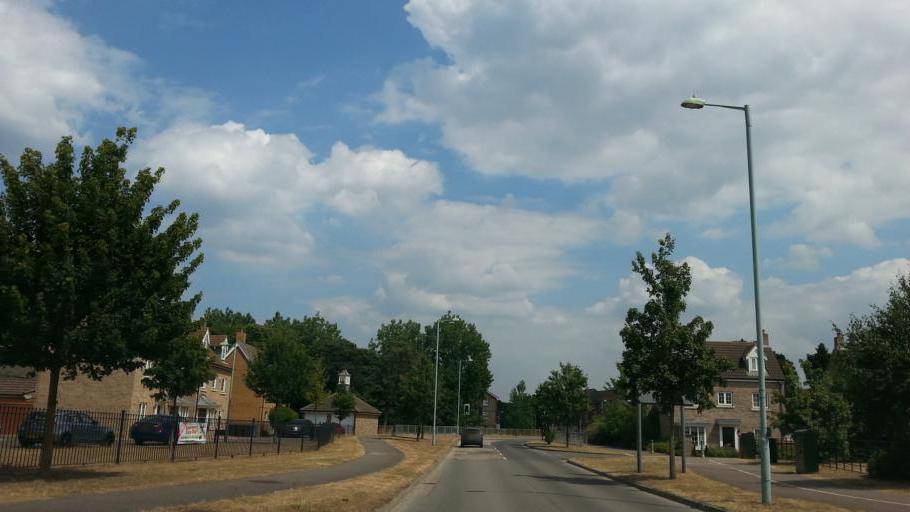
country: GB
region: England
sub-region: Cambridgeshire
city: Isleham
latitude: 52.3090
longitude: 0.4966
